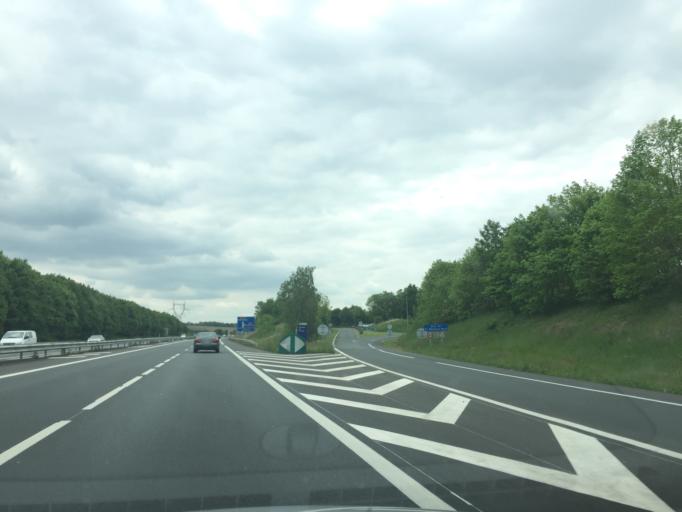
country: FR
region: Poitou-Charentes
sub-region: Departement des Deux-Sevres
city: La Creche
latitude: 46.3572
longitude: -0.2720
